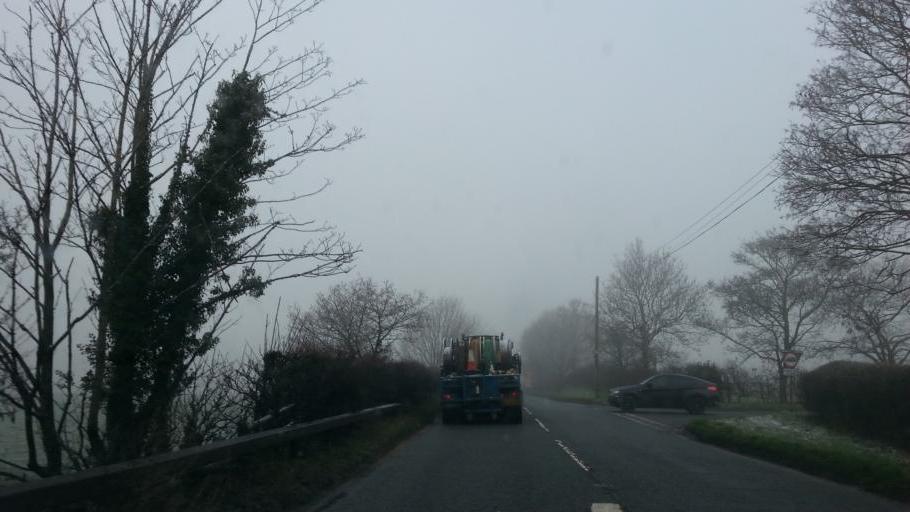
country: GB
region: England
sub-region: Cheshire East
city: Siddington
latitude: 53.2032
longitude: -2.2250
